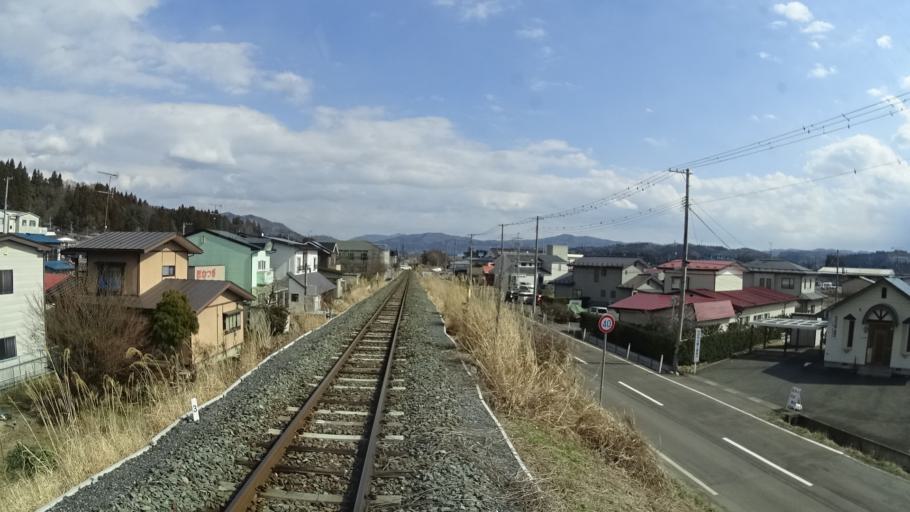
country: JP
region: Iwate
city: Hanamaki
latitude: 39.3855
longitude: 141.2291
